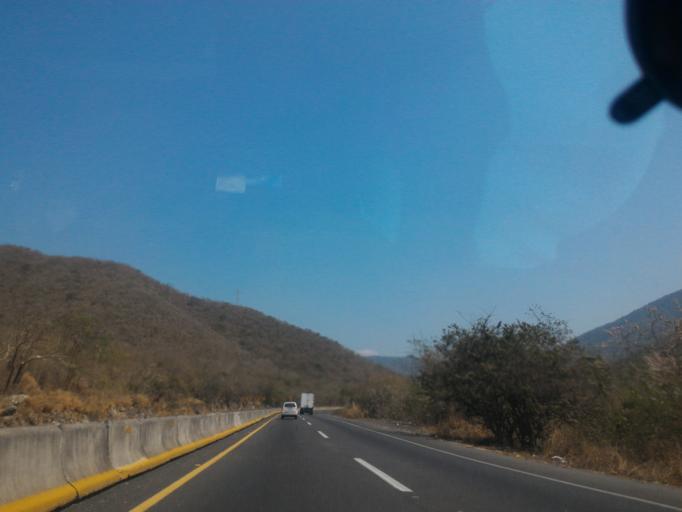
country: MX
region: Colima
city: Ixtlahuacan
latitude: 19.0225
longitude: -103.8148
